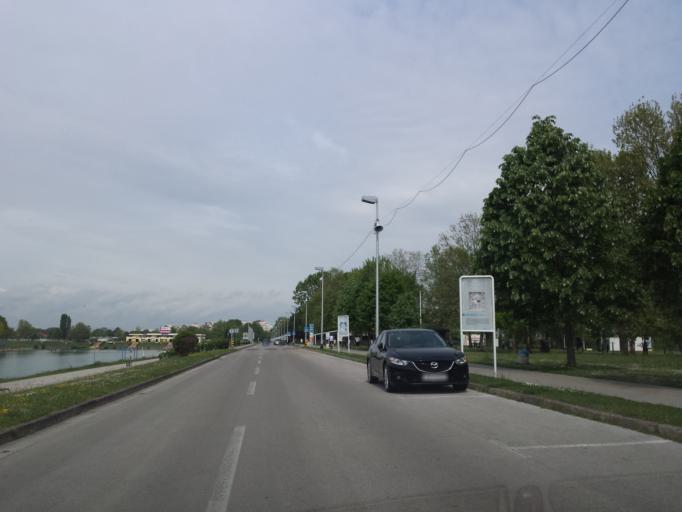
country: HR
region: Grad Zagreb
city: Jankomir
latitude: 45.7848
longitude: 15.9187
